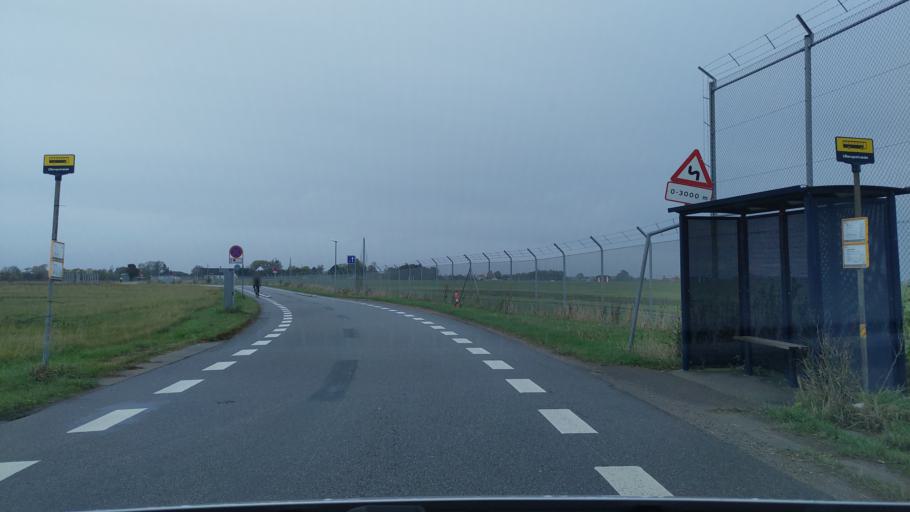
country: DK
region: Capital Region
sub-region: Tarnby Kommune
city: Tarnby
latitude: 55.5867
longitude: 12.5992
